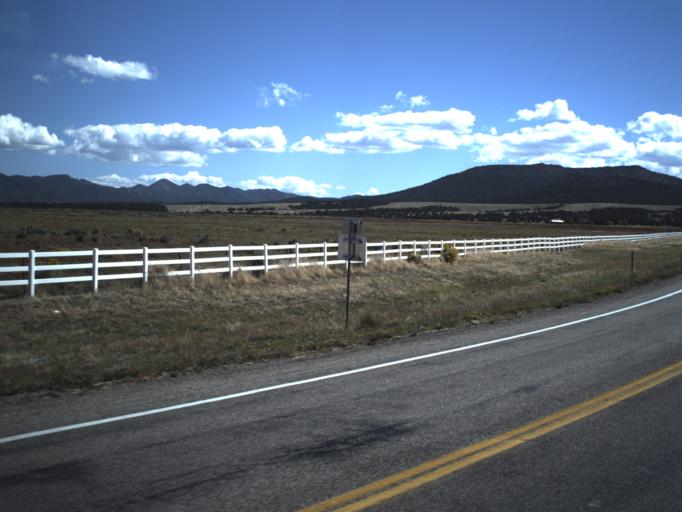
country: US
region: Utah
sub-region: Washington County
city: Enterprise
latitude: 37.5721
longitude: -113.7040
